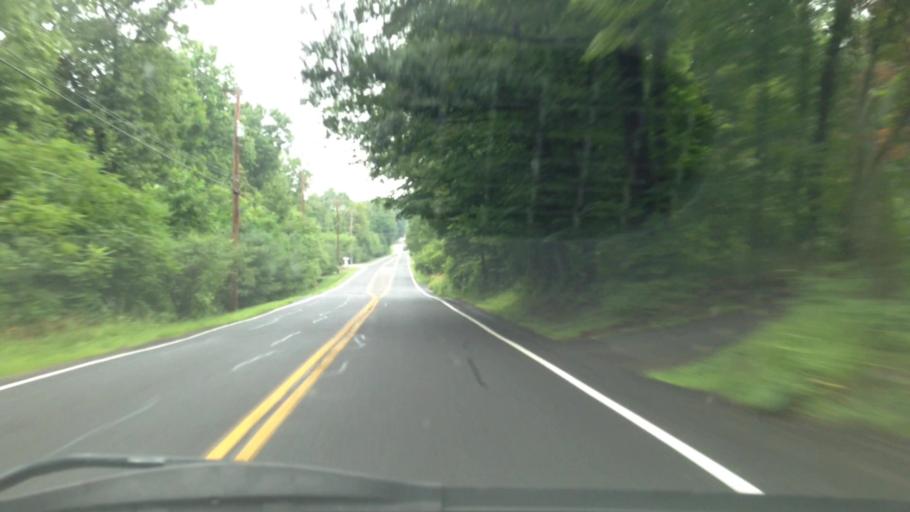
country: US
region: New York
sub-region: Ulster County
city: New Paltz
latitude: 41.7556
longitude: -74.0608
